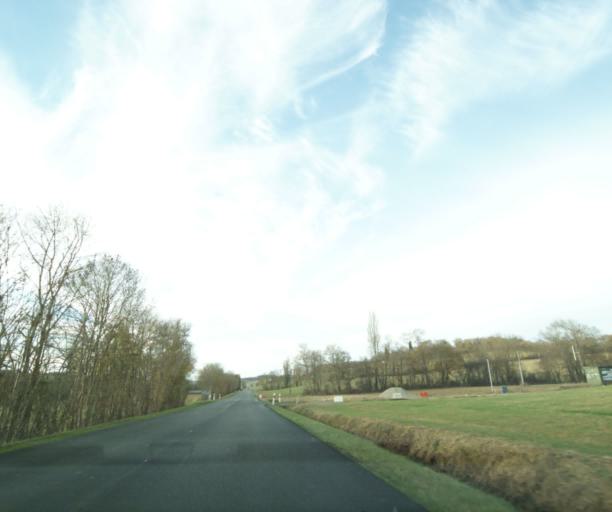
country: FR
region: Midi-Pyrenees
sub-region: Departement du Gers
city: Jegun
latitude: 43.6829
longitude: 0.4936
